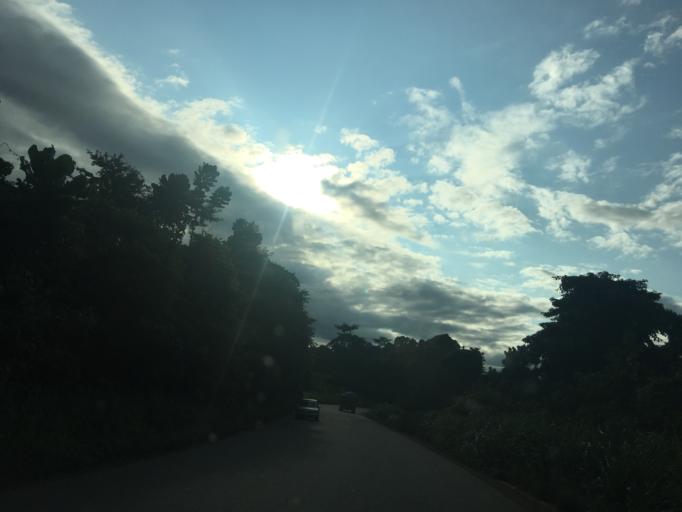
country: GH
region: Western
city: Bibiani
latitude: 6.2838
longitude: -2.2278
